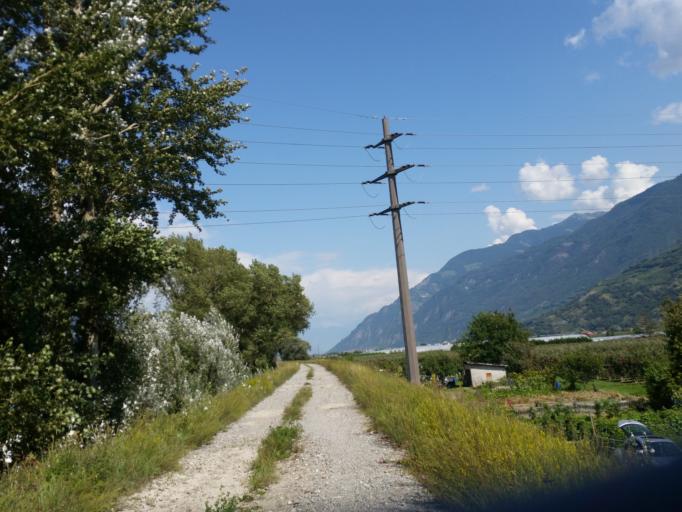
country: CH
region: Valais
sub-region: Martigny District
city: Fully
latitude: 46.1371
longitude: 7.1299
